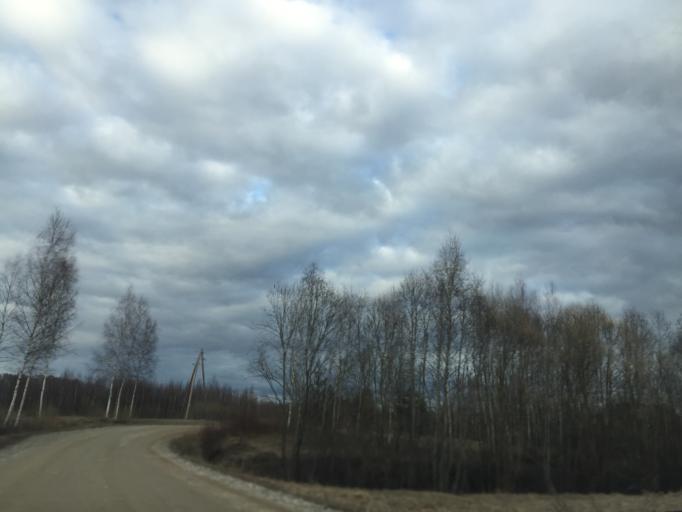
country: LV
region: Jaunjelgava
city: Jaunjelgava
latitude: 56.5966
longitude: 25.0533
